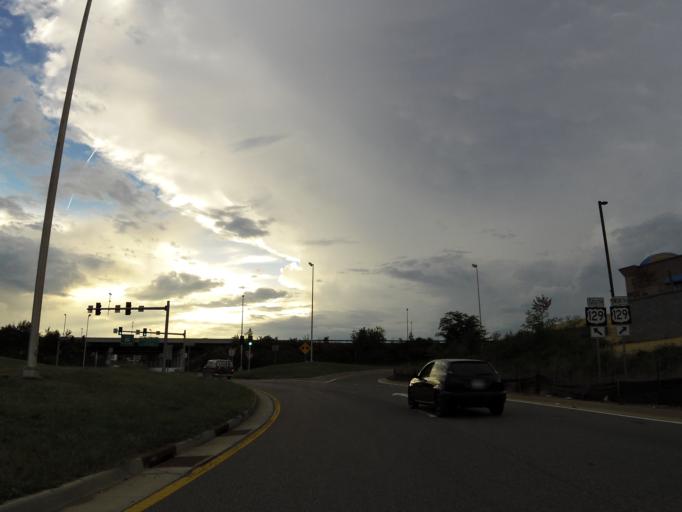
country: US
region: Tennessee
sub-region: Blount County
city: Maryville
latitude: 35.7656
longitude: -83.9855
